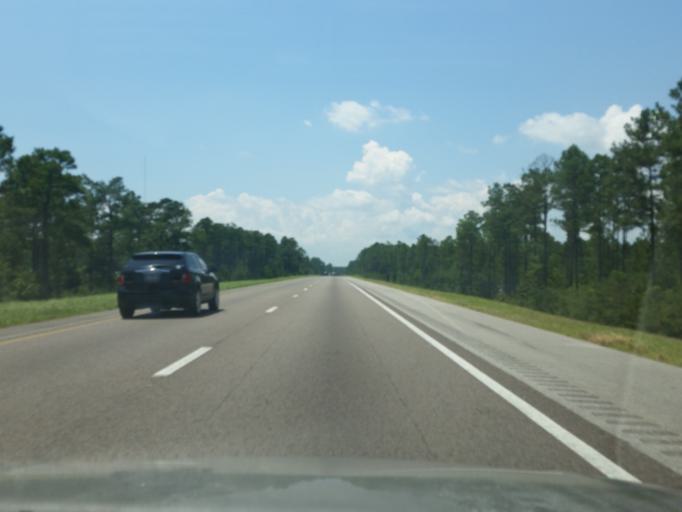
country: US
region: Florida
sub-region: Escambia County
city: Cantonment
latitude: 30.5840
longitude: -87.5234
